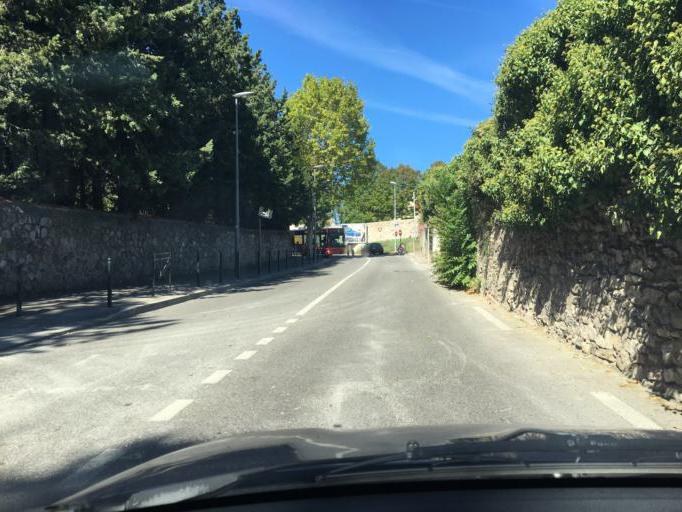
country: FR
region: Provence-Alpes-Cote d'Azur
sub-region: Departement des Bouches-du-Rhone
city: Aix-en-Provence
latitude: 43.5299
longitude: 5.4358
